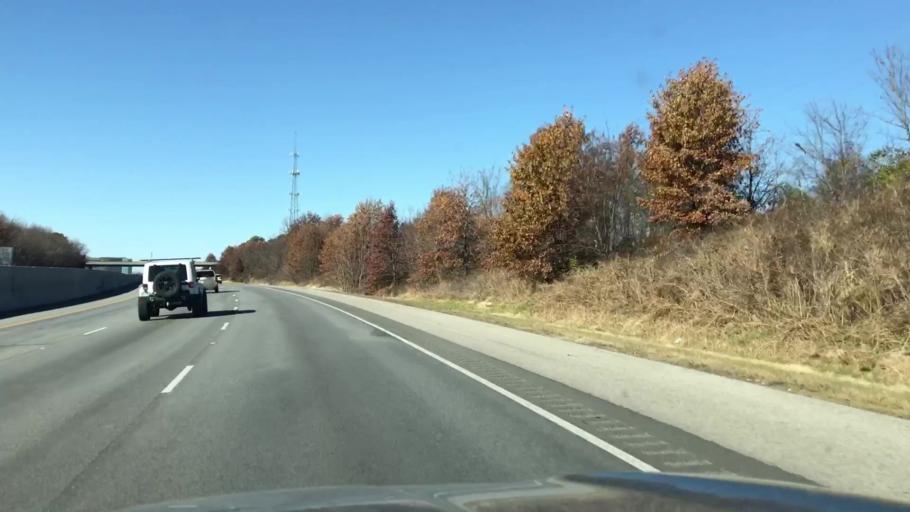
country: US
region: Arkansas
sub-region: Benton County
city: Lowell
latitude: 36.2958
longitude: -94.1672
